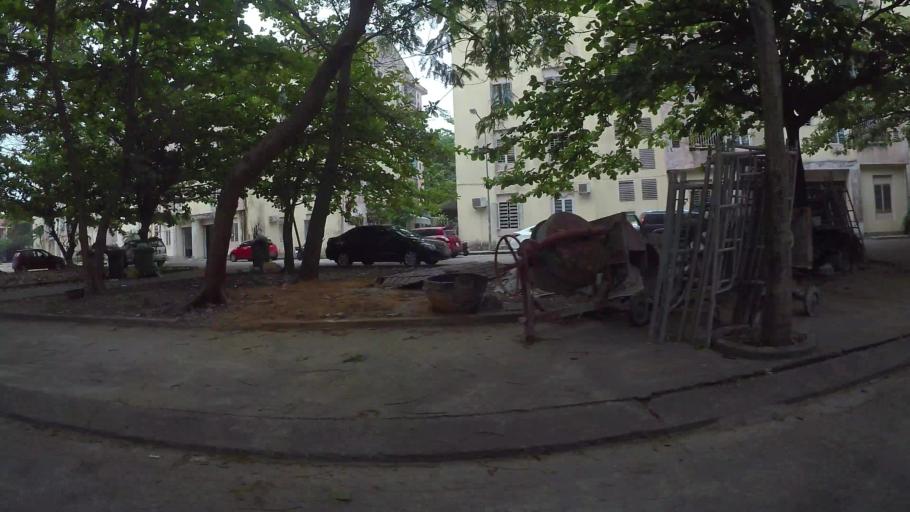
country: VN
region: Da Nang
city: Cam Le
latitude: 16.0298
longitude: 108.2118
